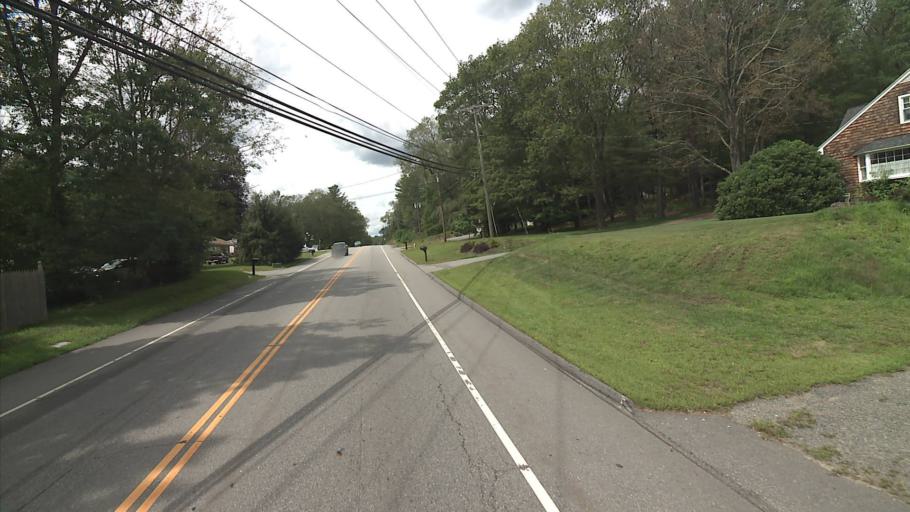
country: US
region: Connecticut
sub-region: Windham County
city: Putnam
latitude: 41.9303
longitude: -71.9277
